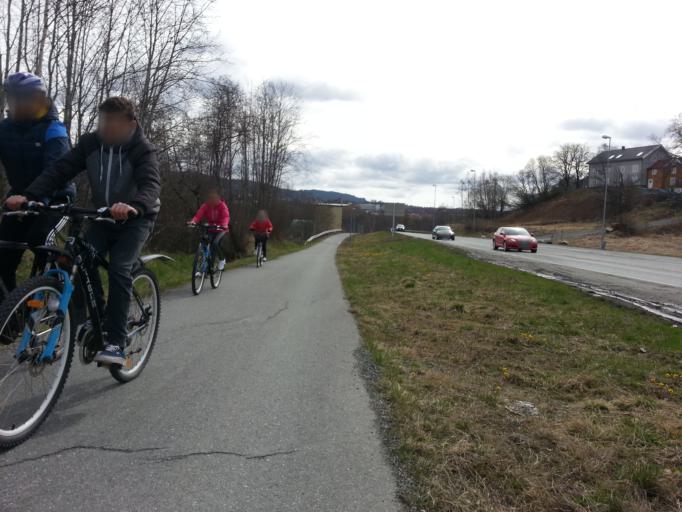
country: NO
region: Sor-Trondelag
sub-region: Trondheim
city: Trondheim
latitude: 63.4092
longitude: 10.3842
